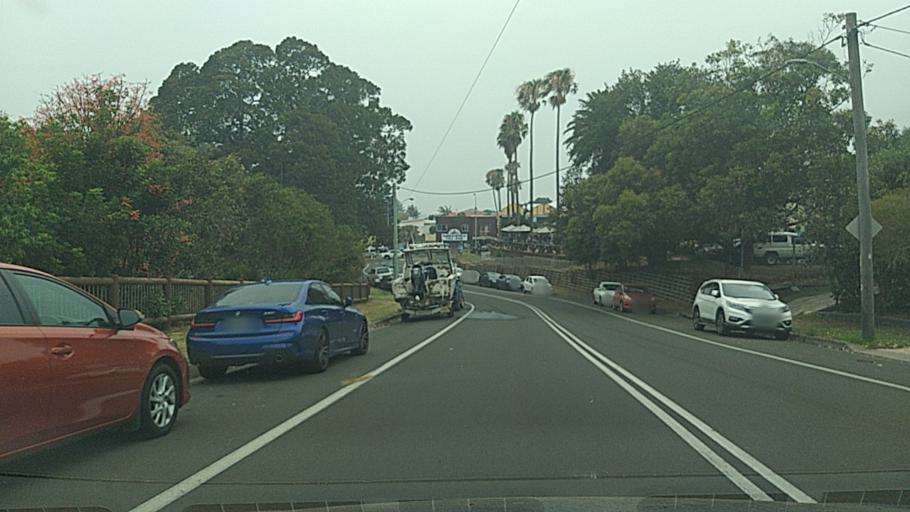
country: AU
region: New South Wales
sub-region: Shellharbour
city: Shellharbour Village
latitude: -34.5773
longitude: 150.8695
